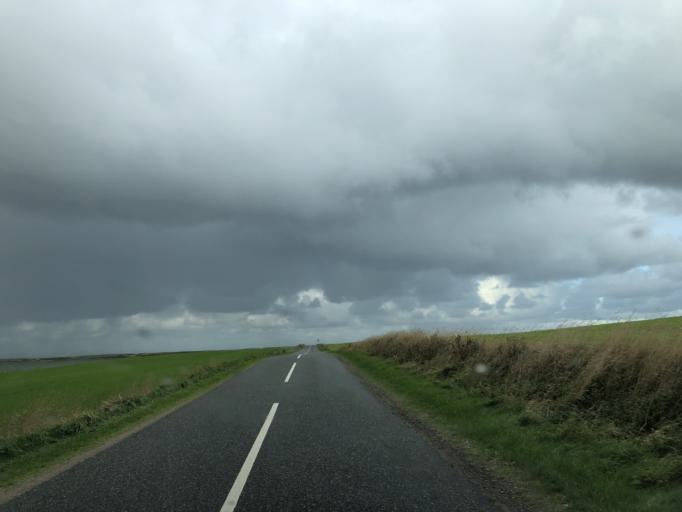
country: DK
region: Central Jutland
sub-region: Lemvig Kommune
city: Harboore
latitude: 56.5472
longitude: 8.1464
